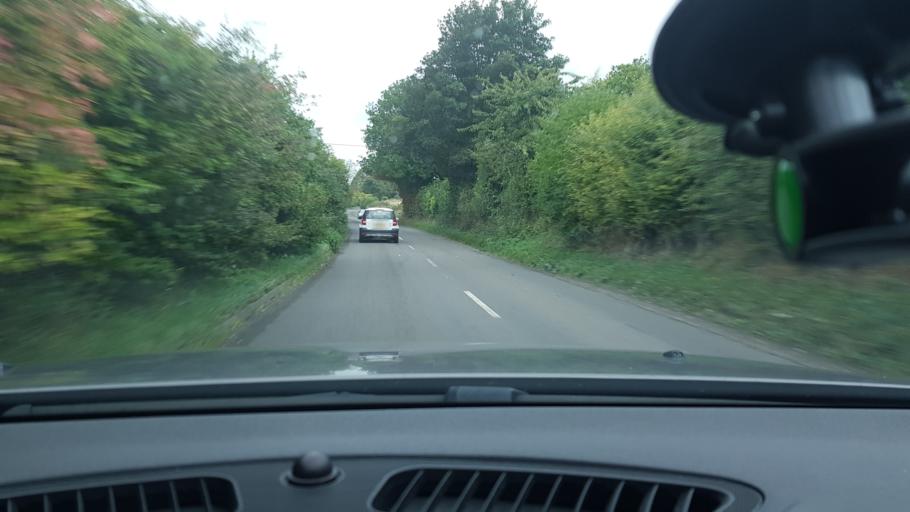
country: GB
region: England
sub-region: Wiltshire
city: Shalbourne
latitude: 51.3618
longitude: -1.5641
